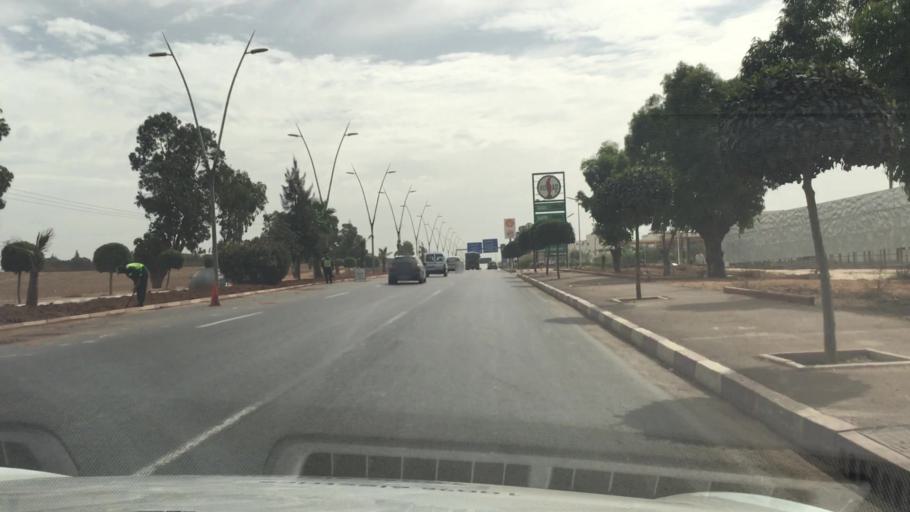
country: MA
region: Grand Casablanca
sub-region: Nouaceur
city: Bouskoura
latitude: 33.5093
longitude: -7.6303
